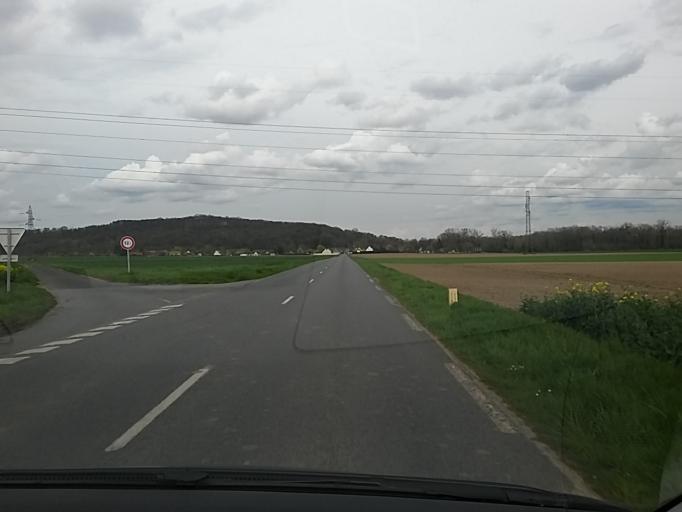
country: FR
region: Picardie
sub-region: Departement de l'Oise
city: Longueil-Sainte-Marie
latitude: 49.3488
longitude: 2.7054
